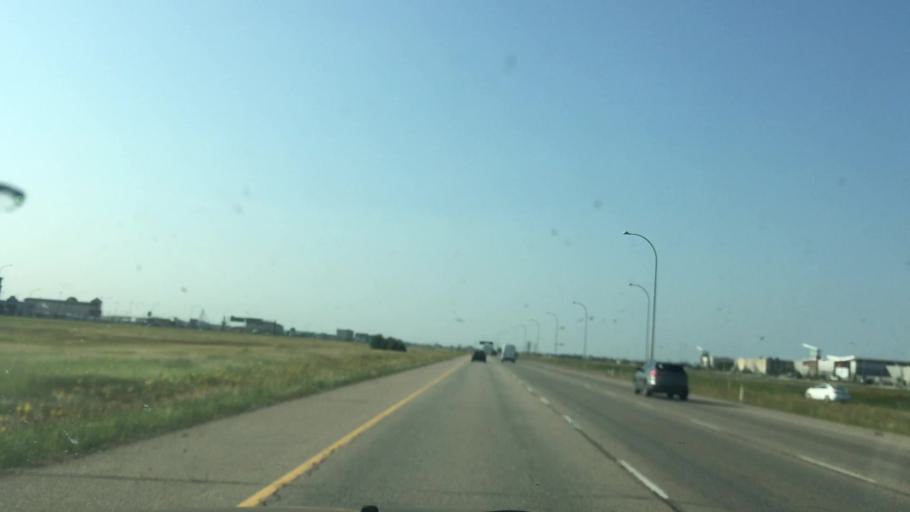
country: CA
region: Alberta
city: Leduc
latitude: 53.3066
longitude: -113.5498
